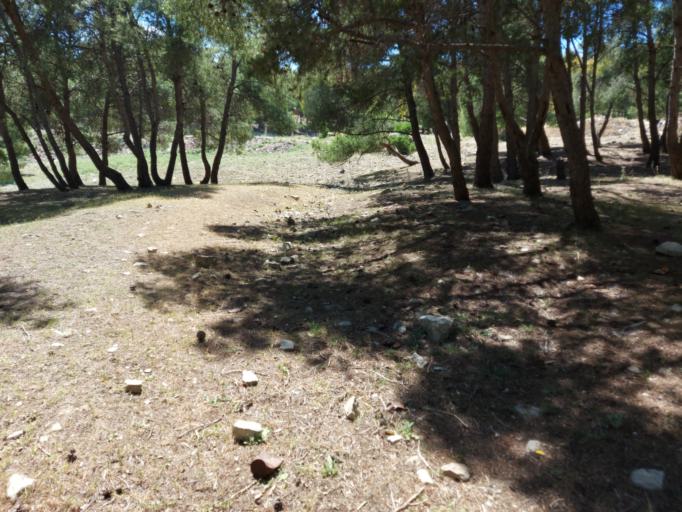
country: TN
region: Kef
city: El Kef
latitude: 36.1852
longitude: 8.7265
